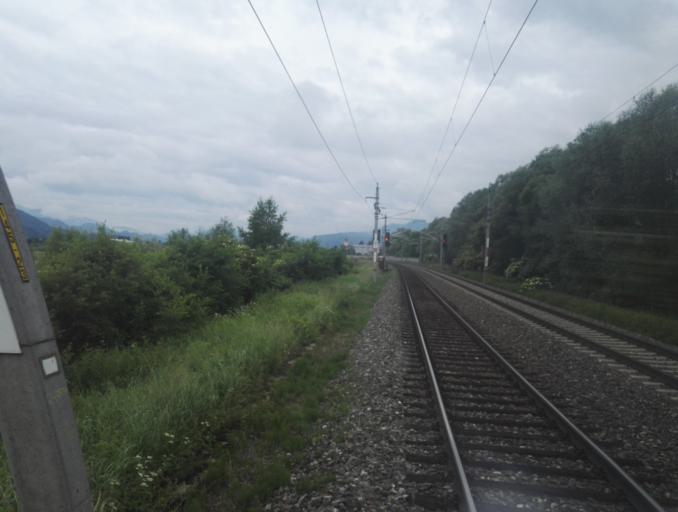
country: AT
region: Styria
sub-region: Politischer Bezirk Bruck-Muerzzuschlag
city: Muerzhofen
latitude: 47.4771
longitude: 15.3858
